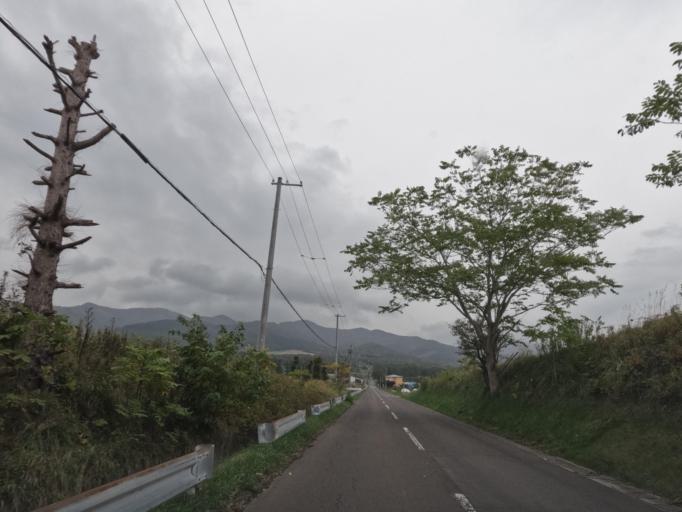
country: JP
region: Hokkaido
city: Date
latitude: 42.4743
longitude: 140.8921
